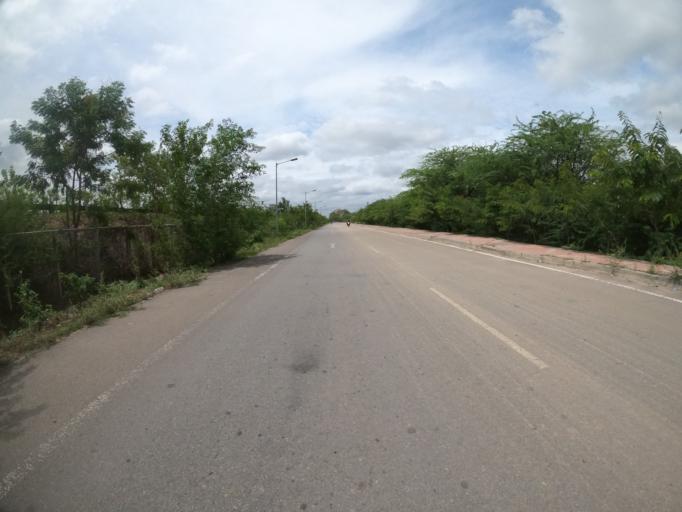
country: IN
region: Telangana
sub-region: Hyderabad
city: Hyderabad
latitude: 17.3024
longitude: 78.3784
